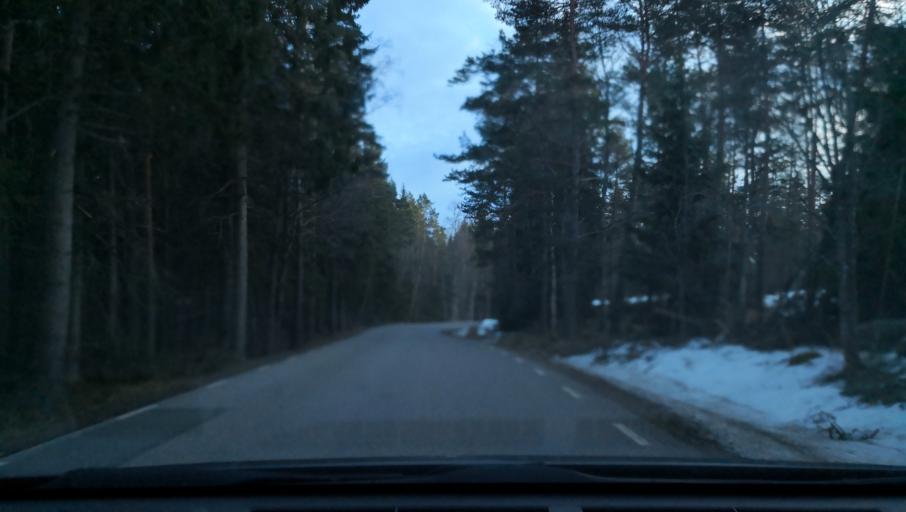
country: SE
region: Uppsala
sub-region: Osthammars Kommun
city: Osterbybruk
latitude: 60.2235
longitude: 17.9187
